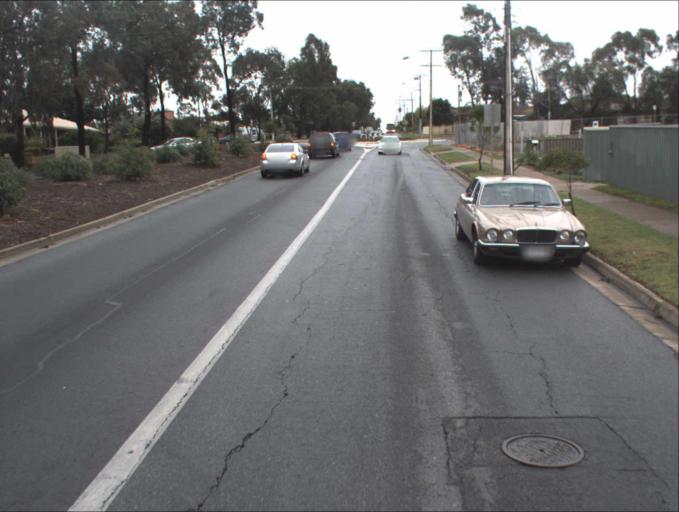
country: AU
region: South Australia
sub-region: Port Adelaide Enfield
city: Gilles Plains
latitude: -34.8359
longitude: 138.6624
